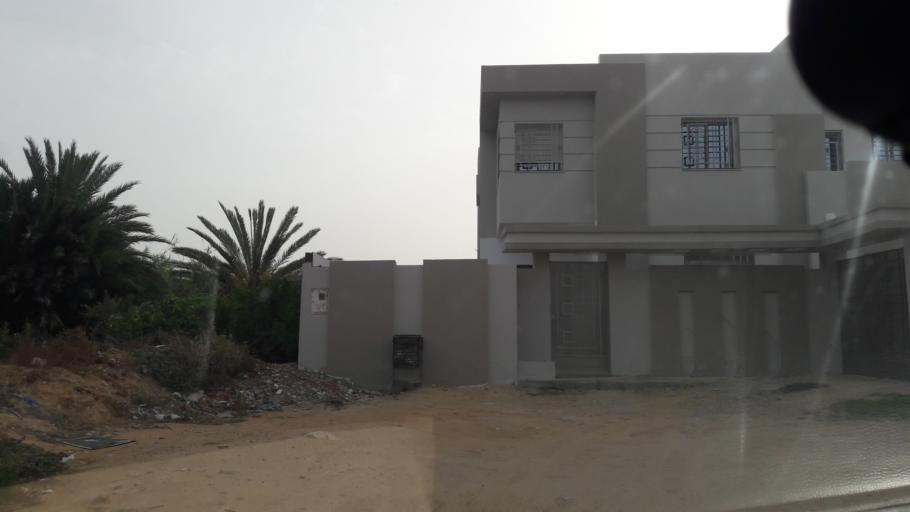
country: TN
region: Safaqis
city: Al Qarmadah
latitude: 34.7789
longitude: 10.7700
